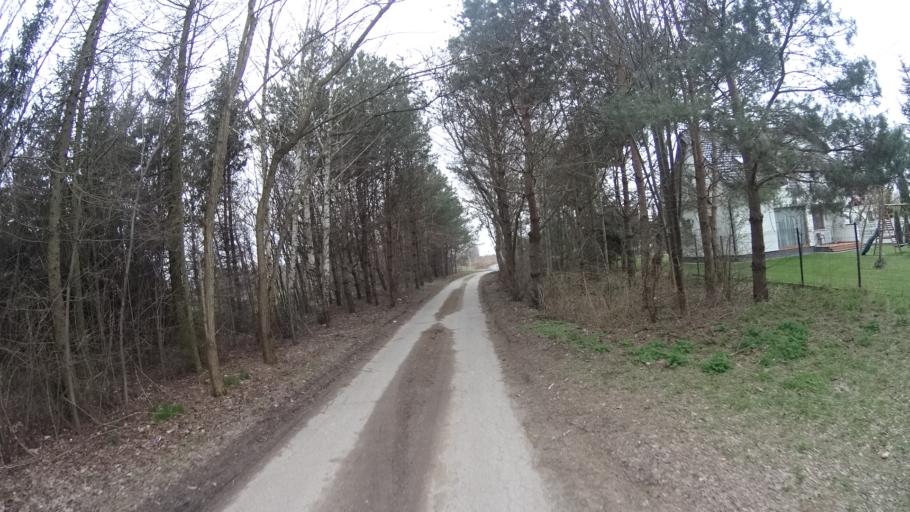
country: PL
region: Masovian Voivodeship
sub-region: Powiat warszawski zachodni
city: Jozefow
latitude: 52.2465
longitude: 20.6737
